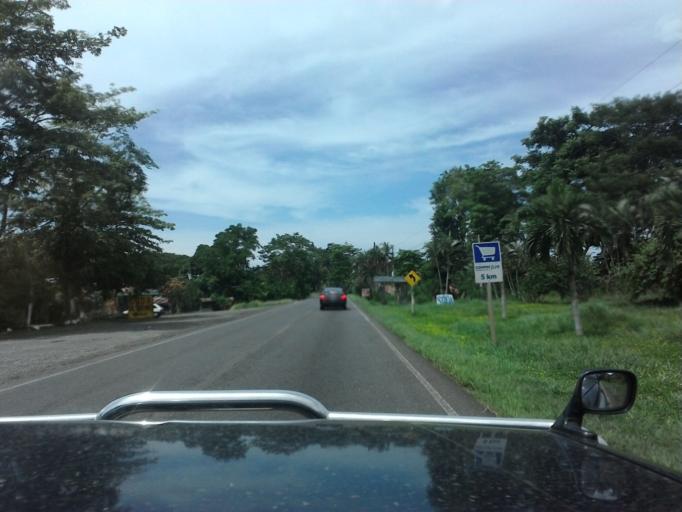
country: CR
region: Puntarenas
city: Esparza
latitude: 10.0084
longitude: -84.6186
